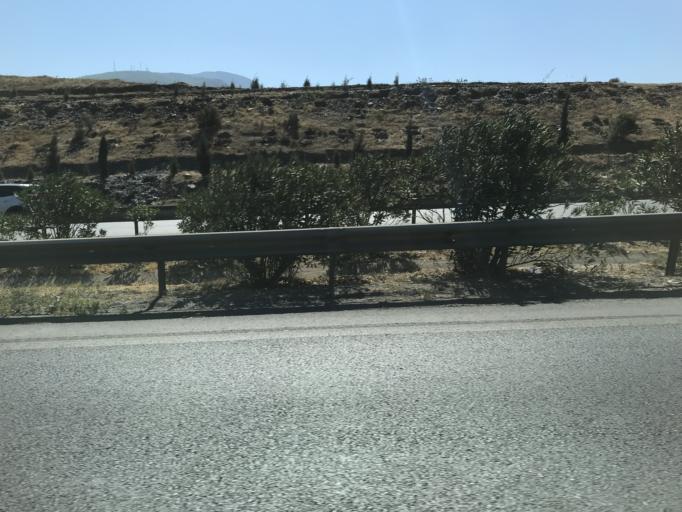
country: TR
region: Izmir
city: Buca
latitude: 38.4026
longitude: 27.2305
